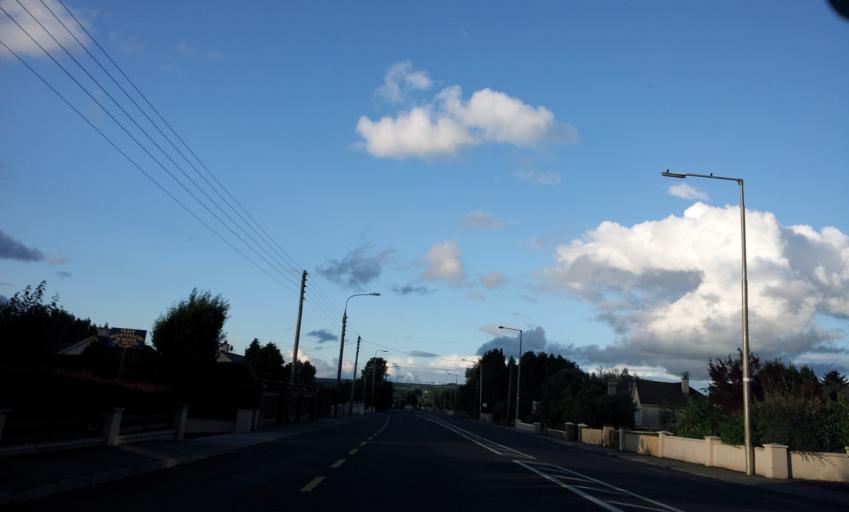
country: IE
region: Munster
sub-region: County Limerick
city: Abbeyfeale
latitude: 52.3756
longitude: -9.3088
